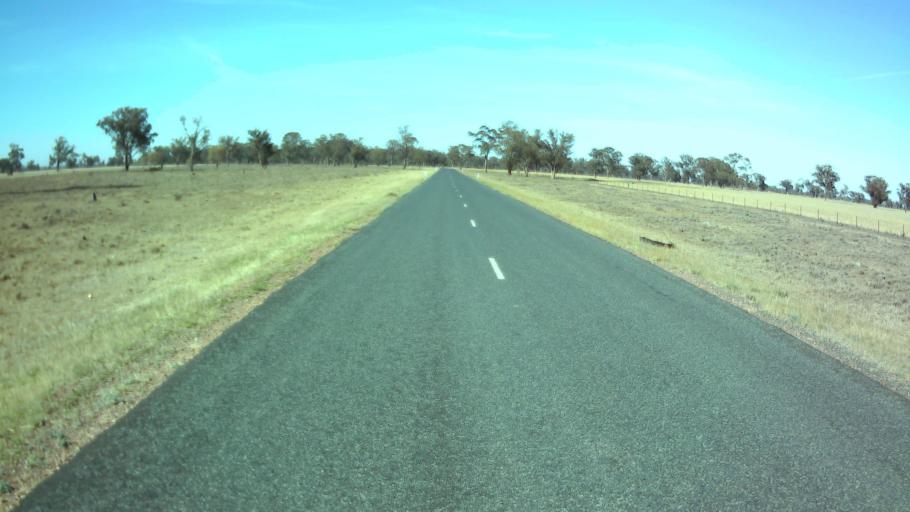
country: AU
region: New South Wales
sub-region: Weddin
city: Grenfell
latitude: -34.0556
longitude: 147.9145
